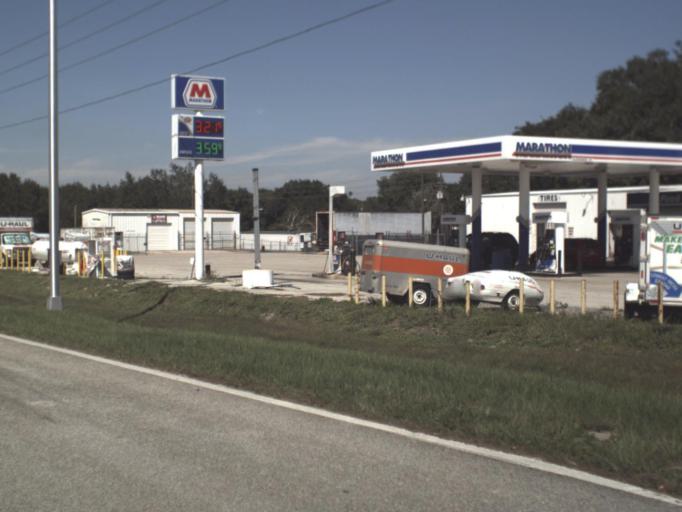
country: US
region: Florida
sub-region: Highlands County
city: Lake Placid
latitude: 27.2695
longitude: -81.3490
